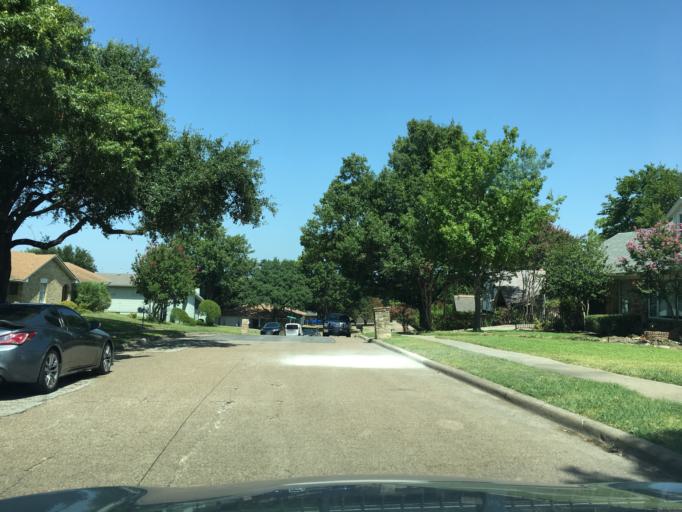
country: US
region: Texas
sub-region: Dallas County
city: Garland
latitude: 32.8741
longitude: -96.6064
